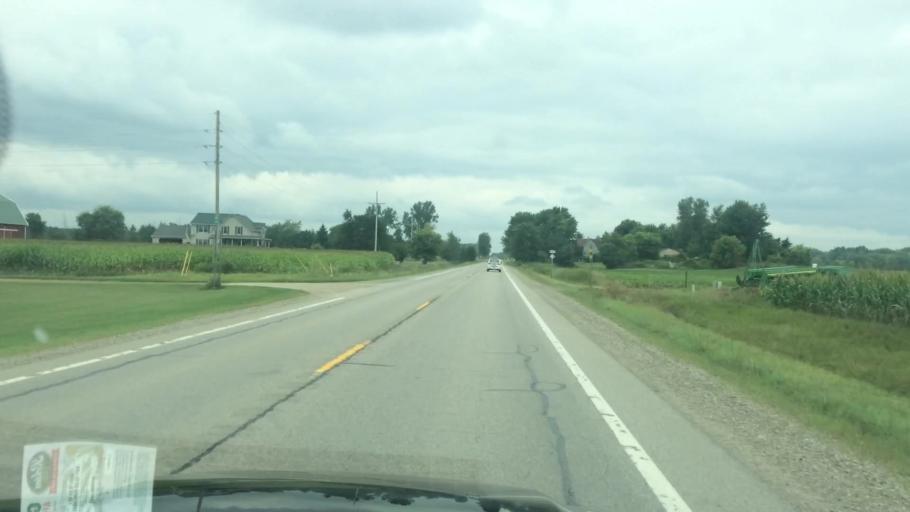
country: US
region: Michigan
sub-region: Sanilac County
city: Marlette
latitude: 43.4359
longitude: -83.0883
